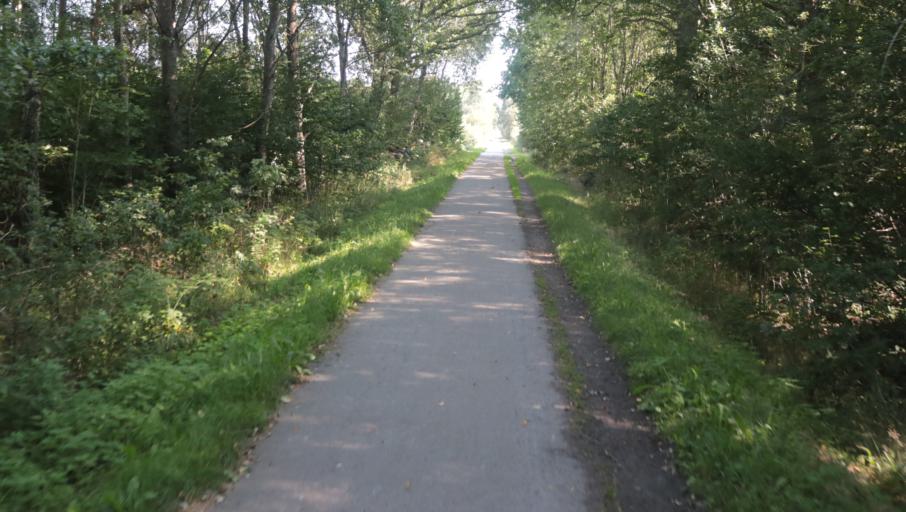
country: SE
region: Blekinge
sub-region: Karlshamns Kommun
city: Svangsta
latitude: 56.2398
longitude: 14.8020
